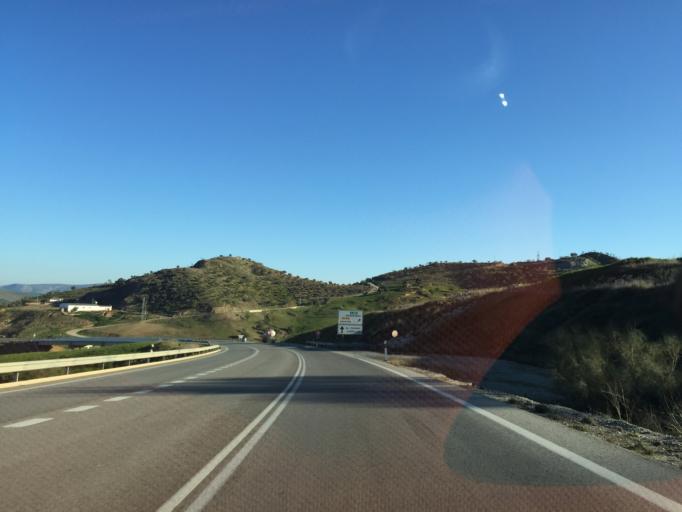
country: ES
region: Andalusia
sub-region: Provincia de Malaga
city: Ardales
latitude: 36.8759
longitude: -4.8371
